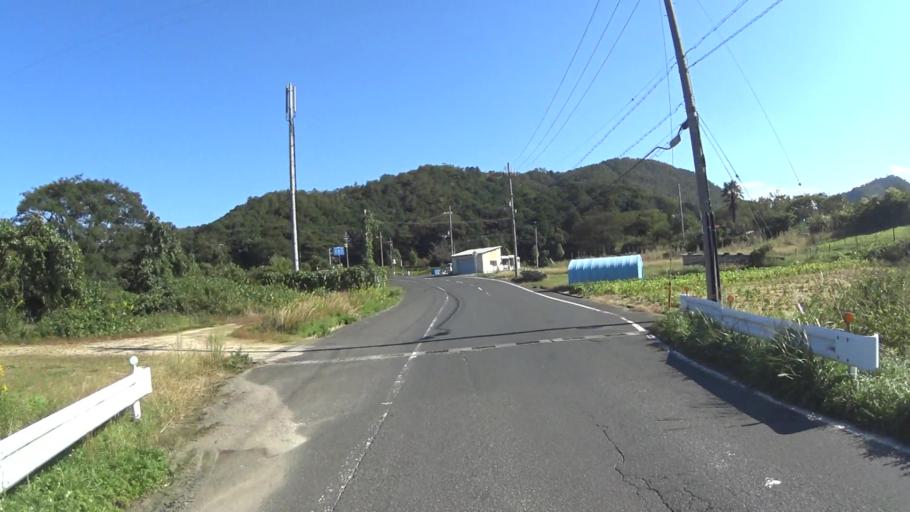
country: JP
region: Hyogo
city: Toyooka
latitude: 35.6278
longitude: 134.9273
